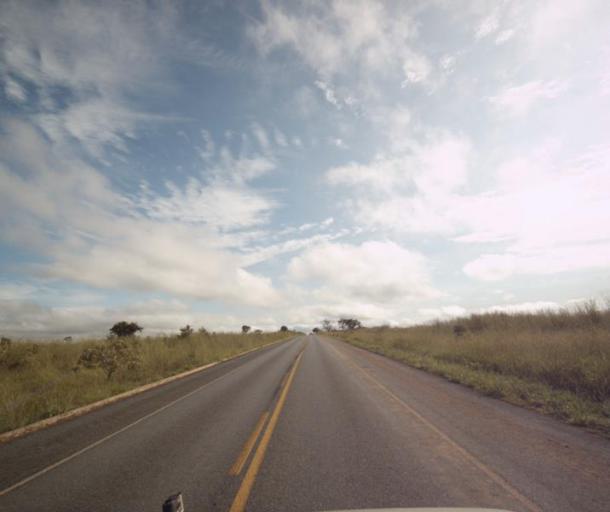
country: BR
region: Goias
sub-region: Padre Bernardo
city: Padre Bernardo
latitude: -15.4691
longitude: -48.6143
